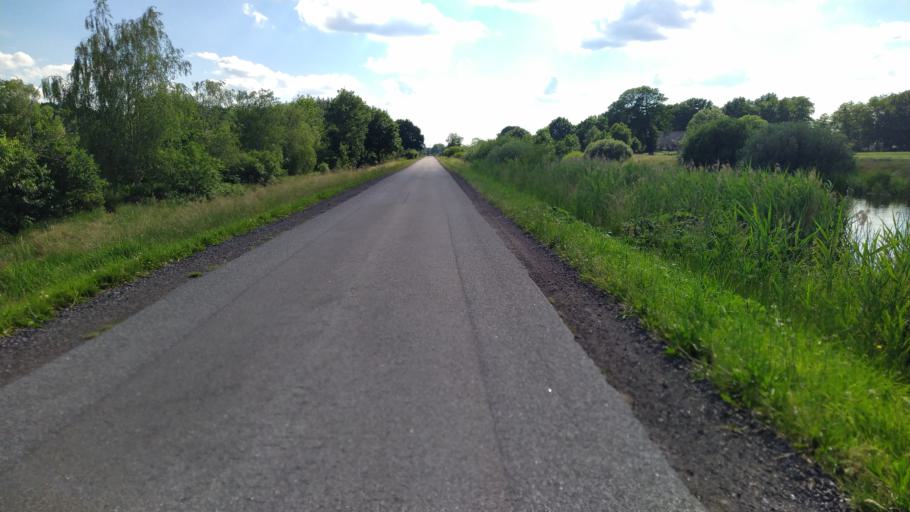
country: DE
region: Lower Saxony
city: Odisheim
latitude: 53.6699
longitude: 8.9151
